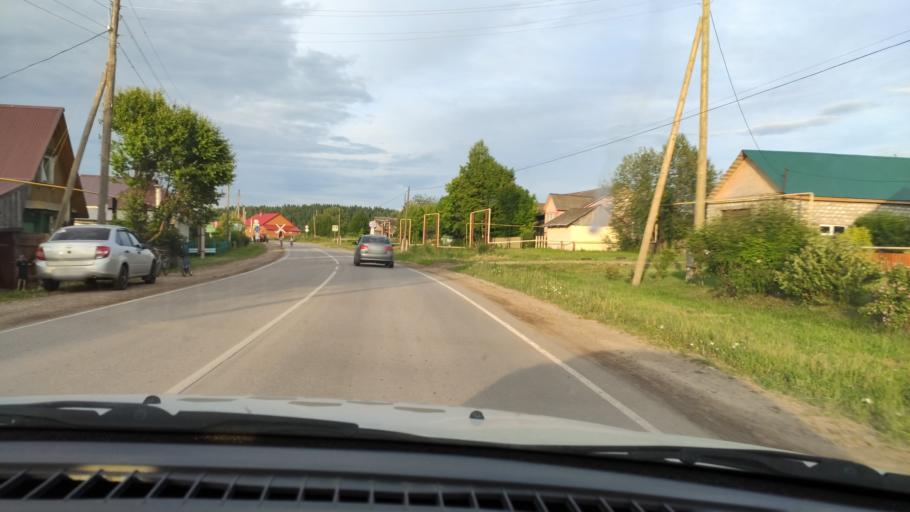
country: RU
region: Perm
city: Kukushtan
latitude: 57.4500
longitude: 56.5151
